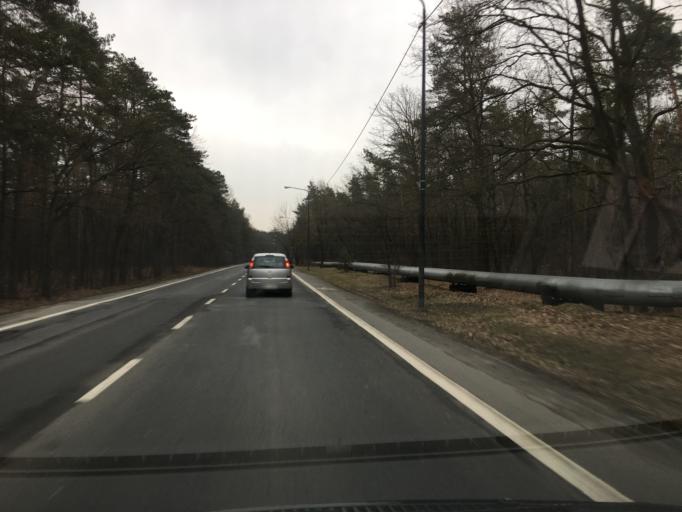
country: PL
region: Opole Voivodeship
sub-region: Powiat kedzierzynsko-kozielski
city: Kedzierzyn-Kozle
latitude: 50.3401
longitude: 18.2292
